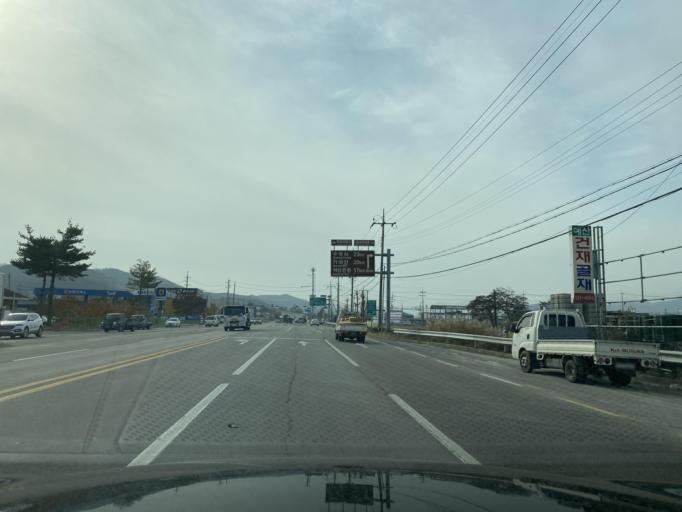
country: KR
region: Chungcheongnam-do
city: Yesan
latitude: 36.6849
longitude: 126.8268
